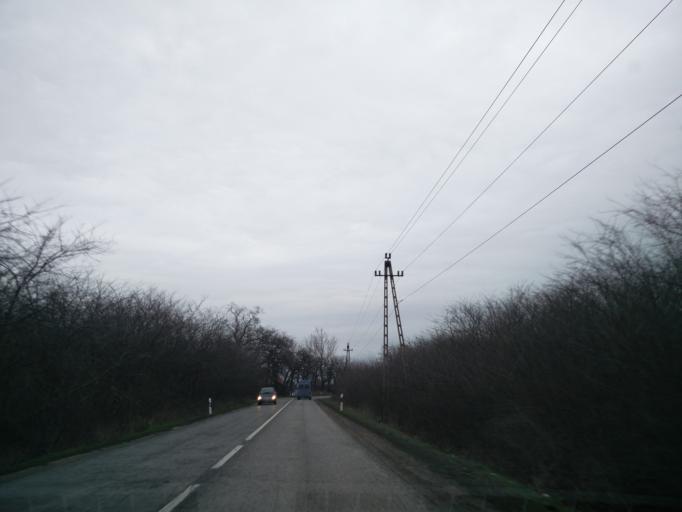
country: HU
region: Pest
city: Ullo
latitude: 47.4031
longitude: 19.3761
